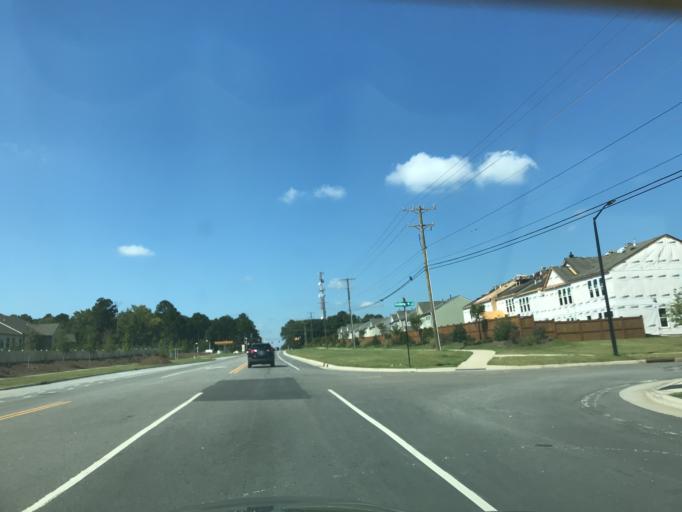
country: US
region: North Carolina
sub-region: Durham County
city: Durham
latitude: 35.9046
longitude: -78.9141
